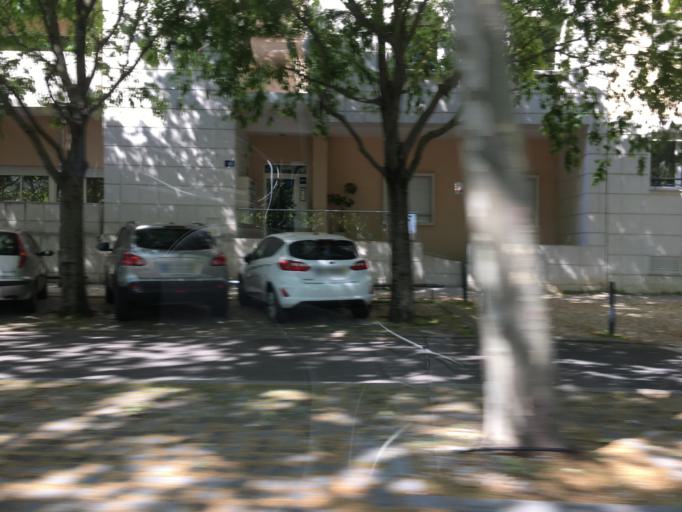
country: PT
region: Lisbon
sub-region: Loures
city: Moscavide
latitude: 38.7805
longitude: -9.0965
